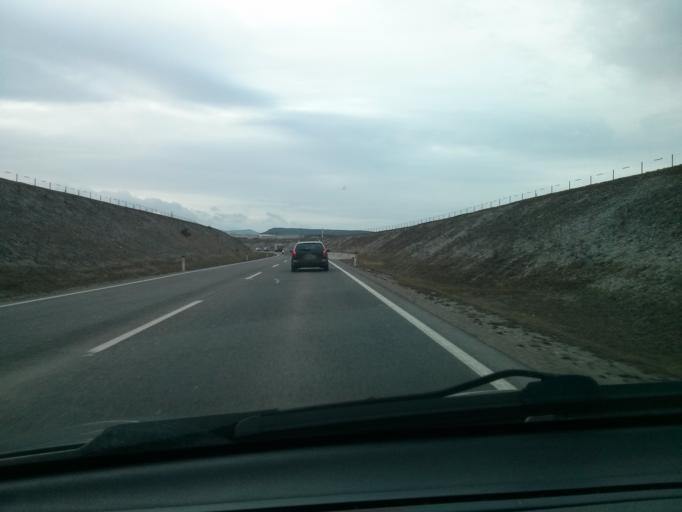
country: AT
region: Lower Austria
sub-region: Politischer Bezirk Wiener Neustadt
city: Theresienfeld
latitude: 47.8512
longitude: 16.2201
